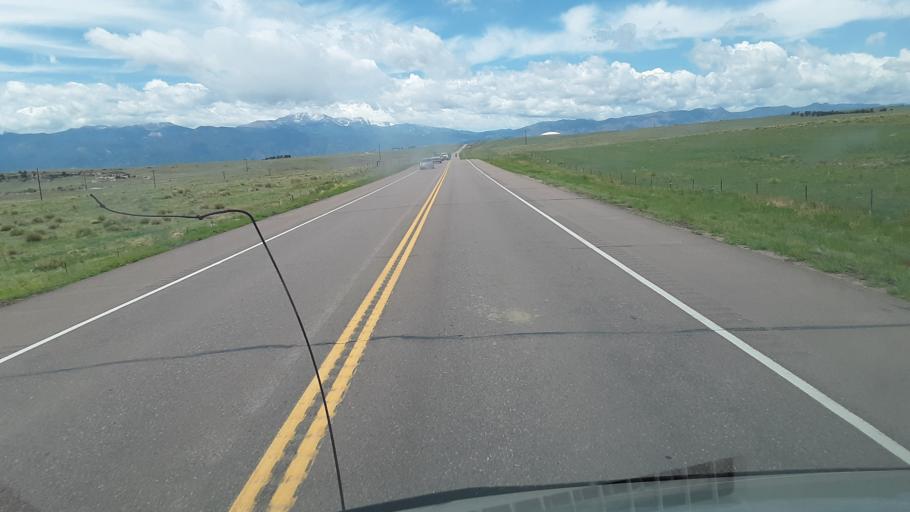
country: US
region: Colorado
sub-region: El Paso County
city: Cimarron Hills
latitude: 38.8352
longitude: -104.6462
